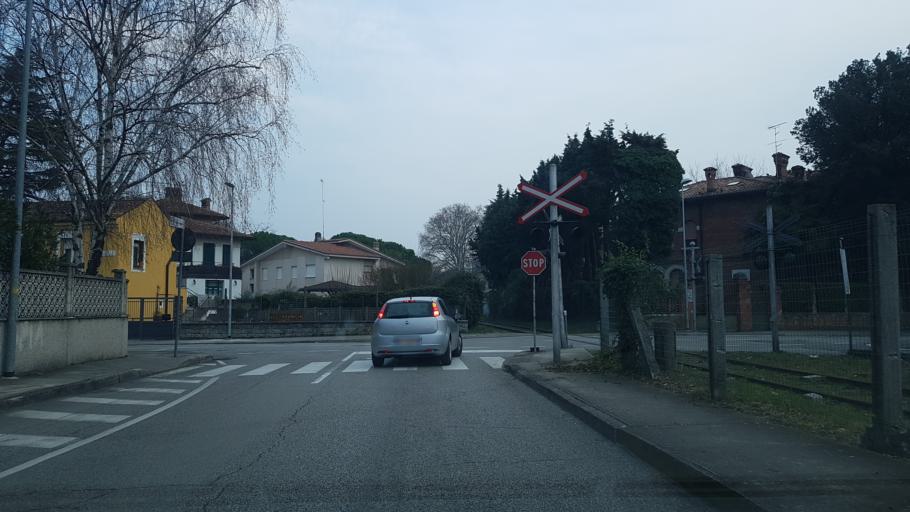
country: IT
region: Friuli Venezia Giulia
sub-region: Provincia di Gorizia
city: Monfalcone
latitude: 45.8040
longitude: 13.5275
